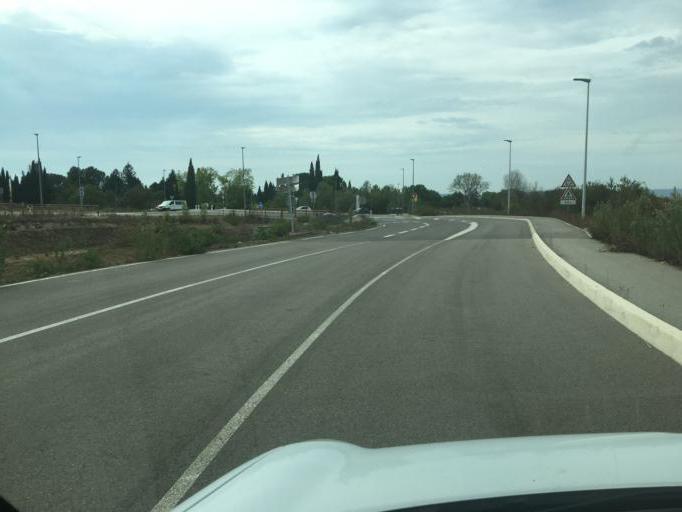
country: FR
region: Provence-Alpes-Cote d'Azur
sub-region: Departement des Bouches-du-Rhone
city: Bouc-Bel-Air
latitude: 43.4727
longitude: 5.4005
